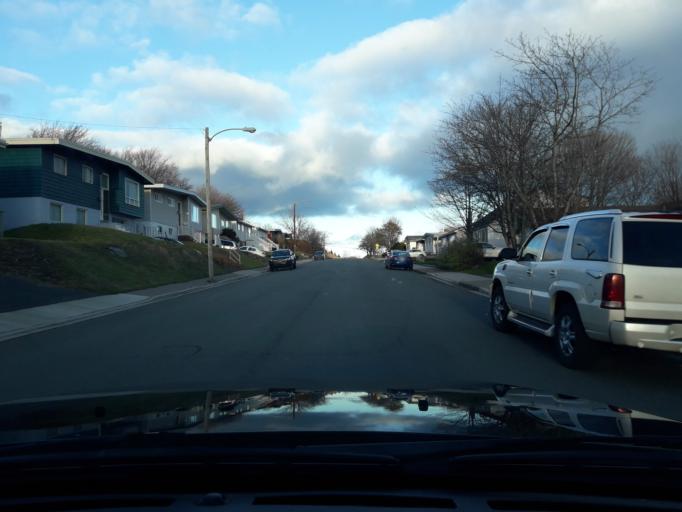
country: CA
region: Newfoundland and Labrador
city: St. John's
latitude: 47.5644
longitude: -52.7569
